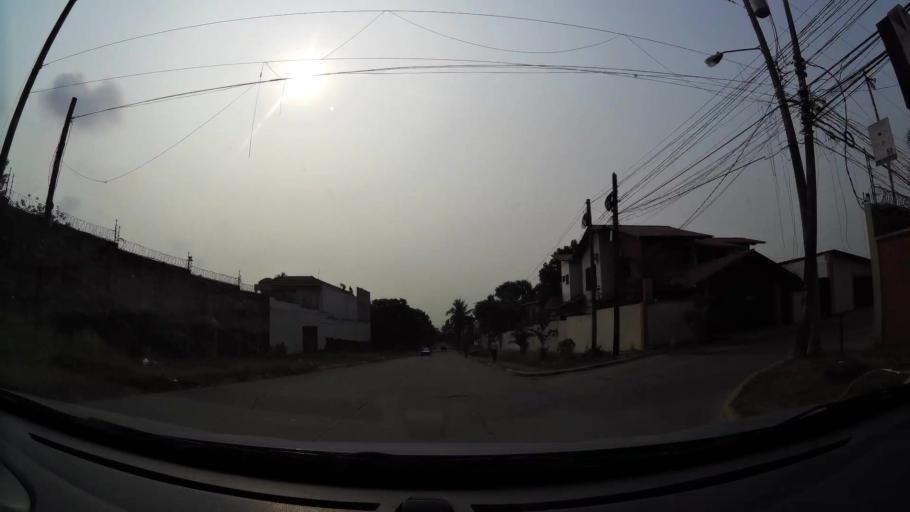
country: HN
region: Cortes
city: Armenta
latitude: 15.4886
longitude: -88.0381
